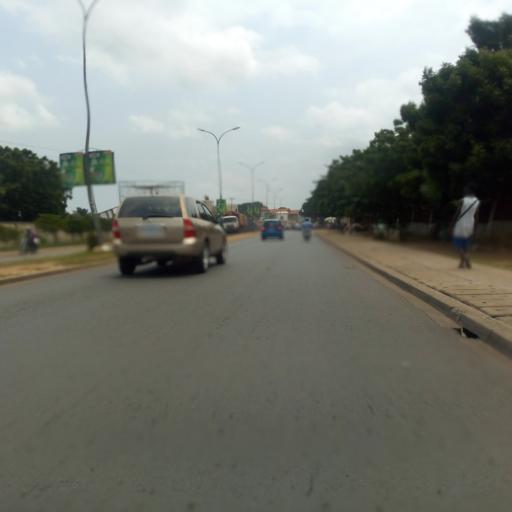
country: TG
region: Maritime
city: Lome
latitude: 6.1893
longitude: 1.1642
